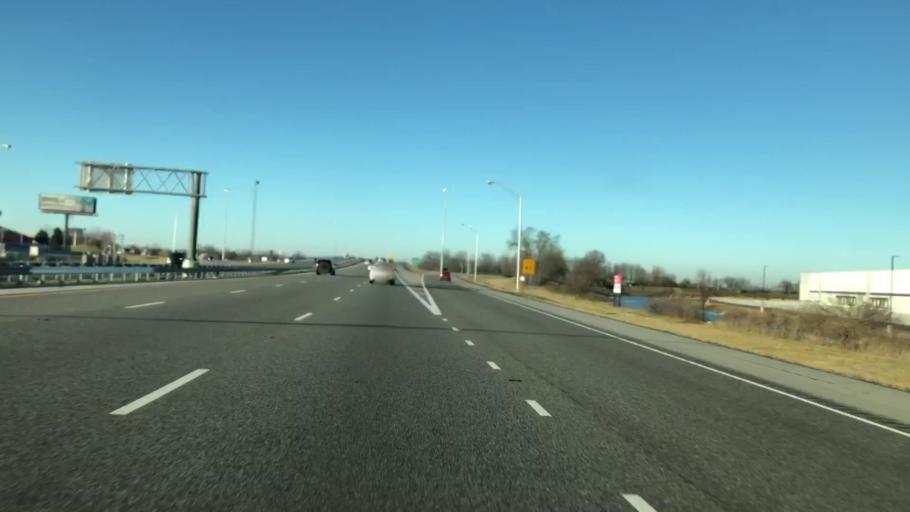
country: US
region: Indiana
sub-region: Johnson County
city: Franklin
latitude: 39.4786
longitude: -86.0124
